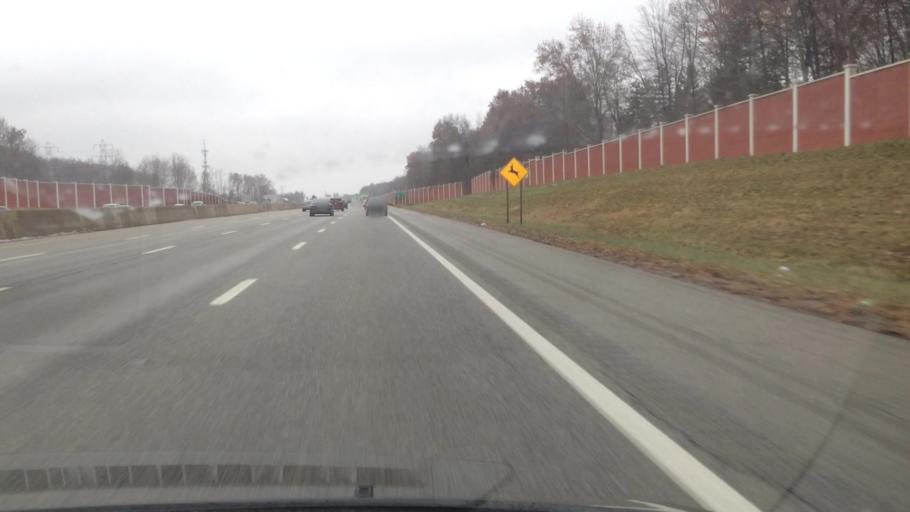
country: US
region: Ohio
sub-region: Cuyahoga County
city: Independence
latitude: 41.3836
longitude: -81.6530
